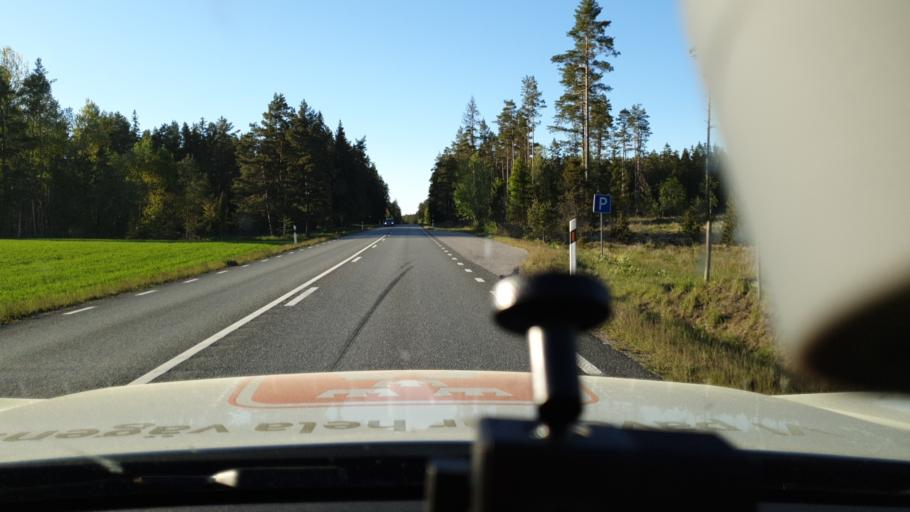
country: SE
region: Joenkoeping
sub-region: Vetlanda Kommun
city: Ekenassjon
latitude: 57.5699
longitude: 14.9732
